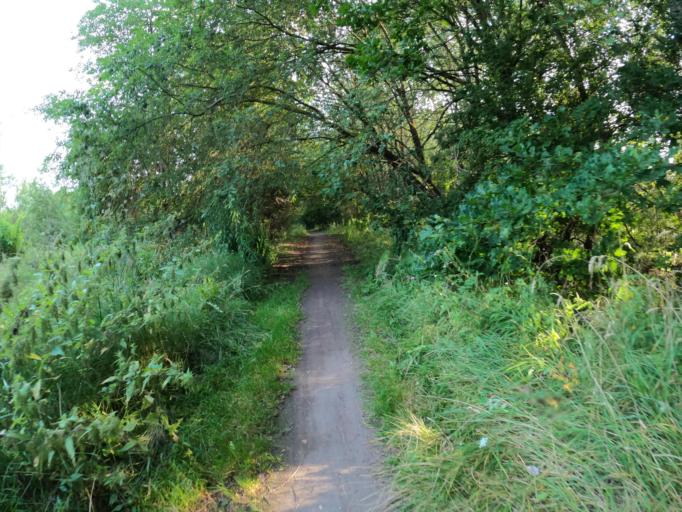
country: PL
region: West Pomeranian Voivodeship
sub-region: Koszalin
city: Koszalin
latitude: 54.1693
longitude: 16.2241
